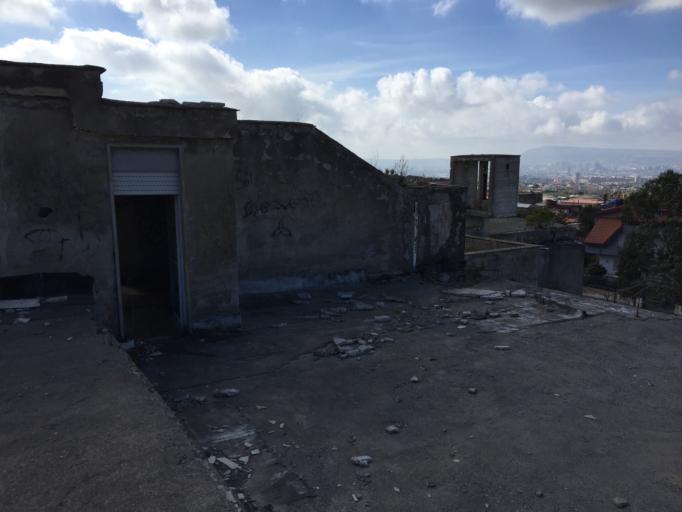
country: IT
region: Campania
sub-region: Provincia di Napoli
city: Pollena Trocchia
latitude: 40.8507
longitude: 14.3790
